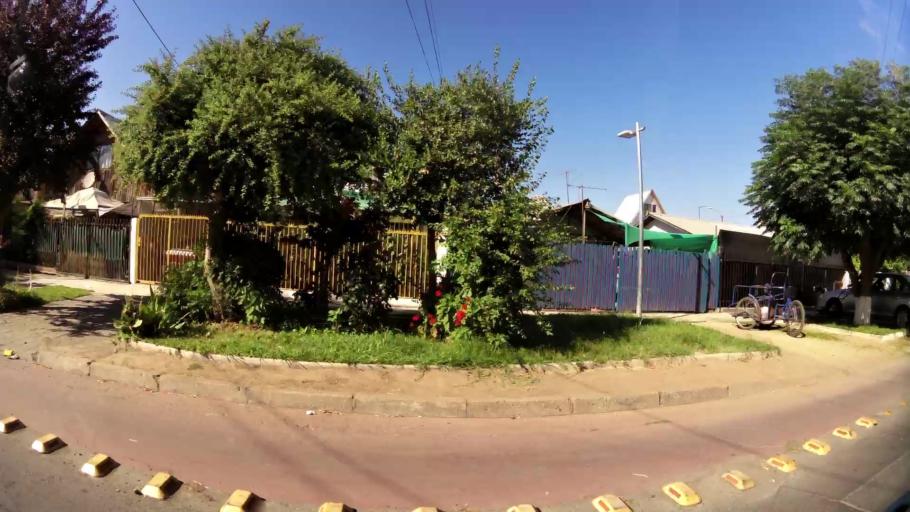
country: CL
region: Maule
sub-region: Provincia de Curico
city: Curico
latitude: -34.9999
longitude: -71.2461
